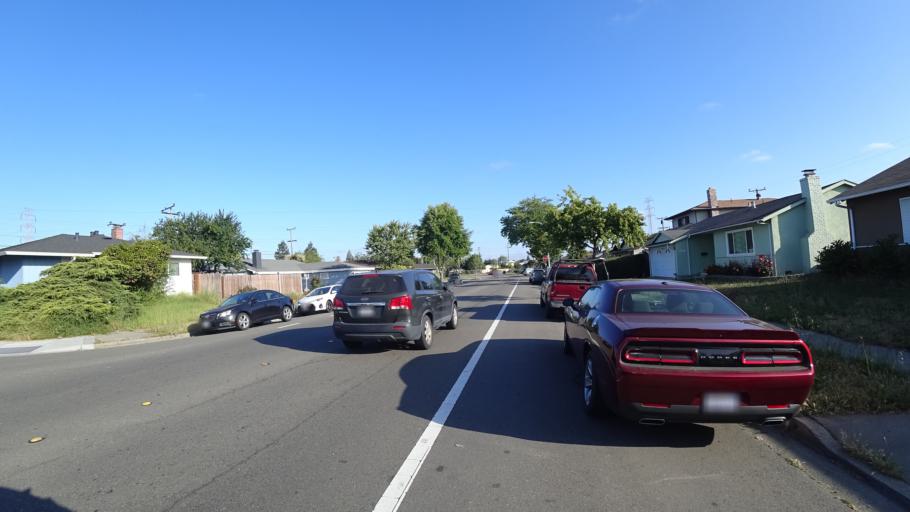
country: US
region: California
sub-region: Alameda County
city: Hayward
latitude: 37.6380
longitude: -122.0907
